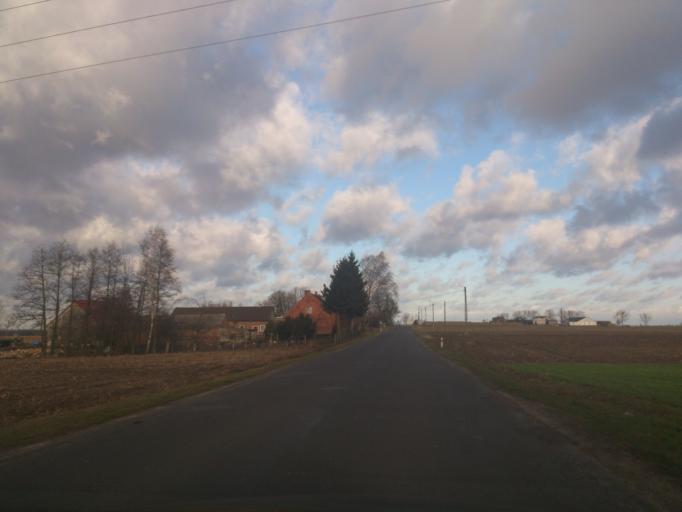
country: PL
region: Kujawsko-Pomorskie
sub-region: Powiat torunski
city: Obrowo
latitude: 53.0234
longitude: 18.8651
